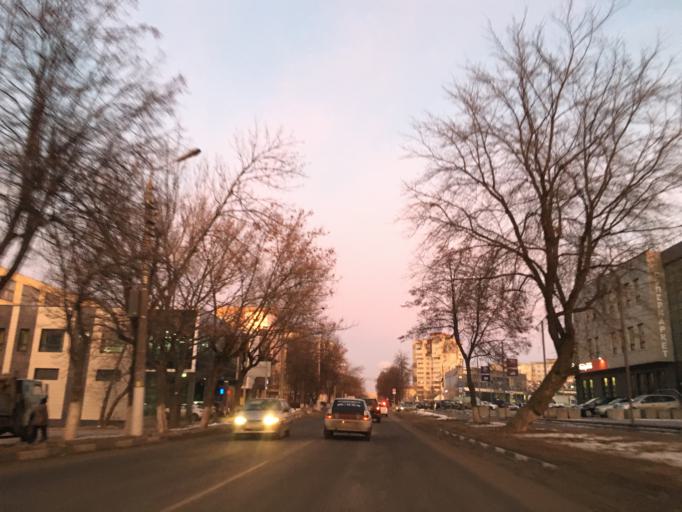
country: RU
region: Tula
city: Tula
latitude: 54.1918
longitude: 37.5975
